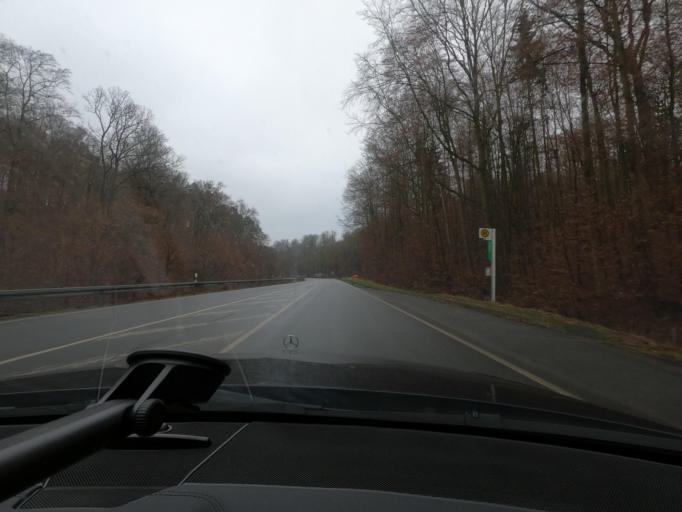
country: DE
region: Hesse
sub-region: Regierungsbezirk Kassel
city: Bad Arolsen
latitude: 51.3589
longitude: 9.0599
